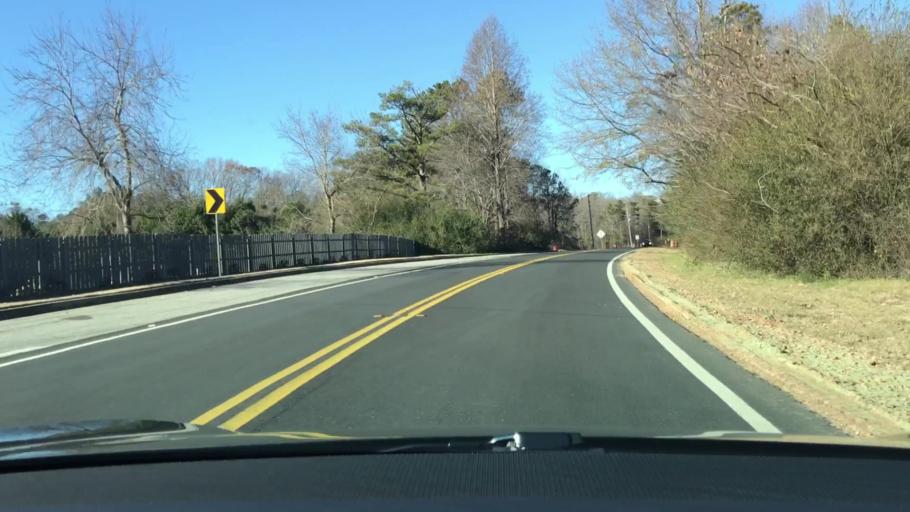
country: US
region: Georgia
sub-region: Barrow County
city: Auburn
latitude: 34.0820
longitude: -83.8673
